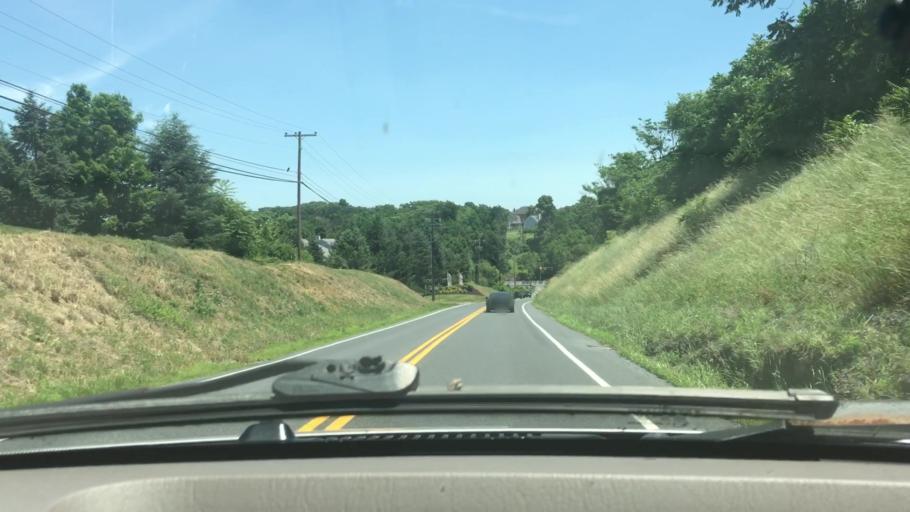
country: US
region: Pennsylvania
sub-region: Dauphin County
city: Rutherford
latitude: 40.2948
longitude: -76.7717
